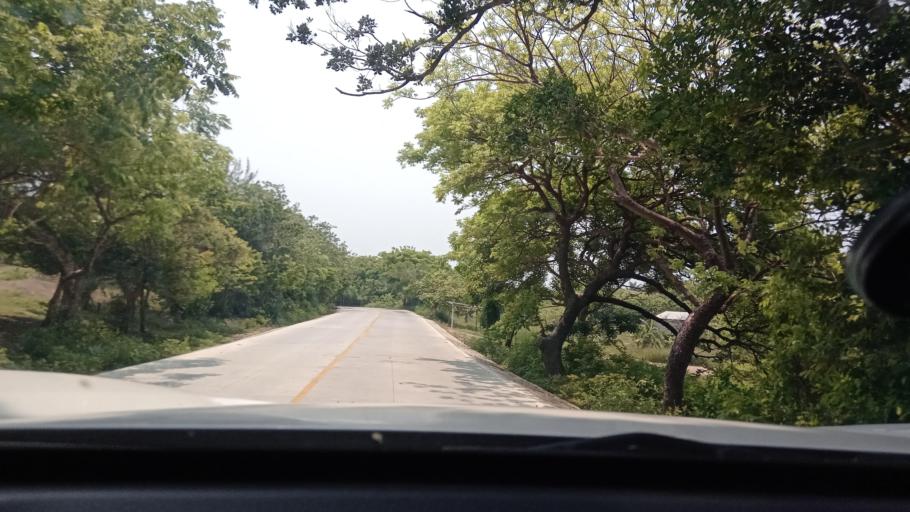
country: MX
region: Veracruz
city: Catemaco
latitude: 18.5575
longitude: -95.0064
